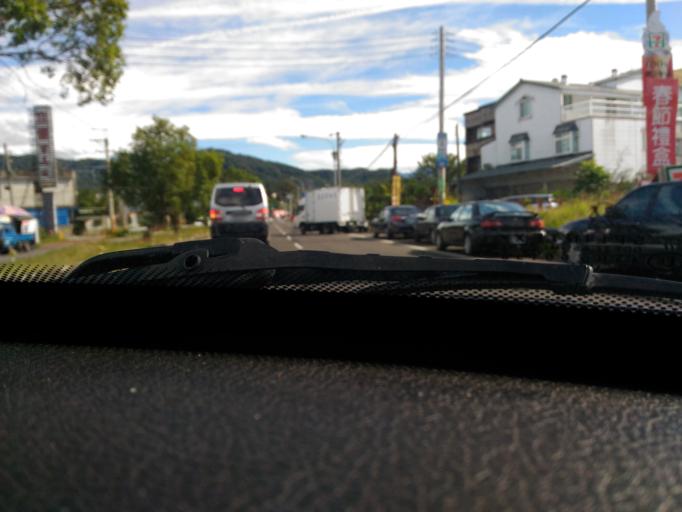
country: TW
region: Taiwan
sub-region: Hsinchu
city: Zhubei
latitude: 24.7643
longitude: 121.0857
